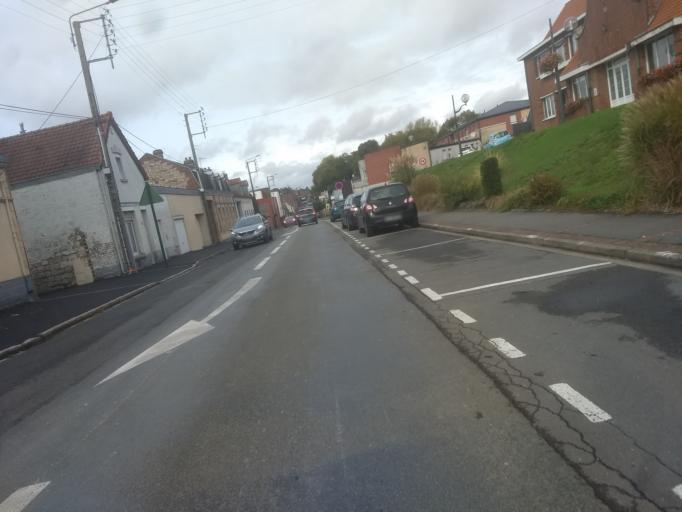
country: FR
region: Nord-Pas-de-Calais
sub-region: Departement du Pas-de-Calais
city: Anzin-Saint-Aubin
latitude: 50.3107
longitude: 2.7501
